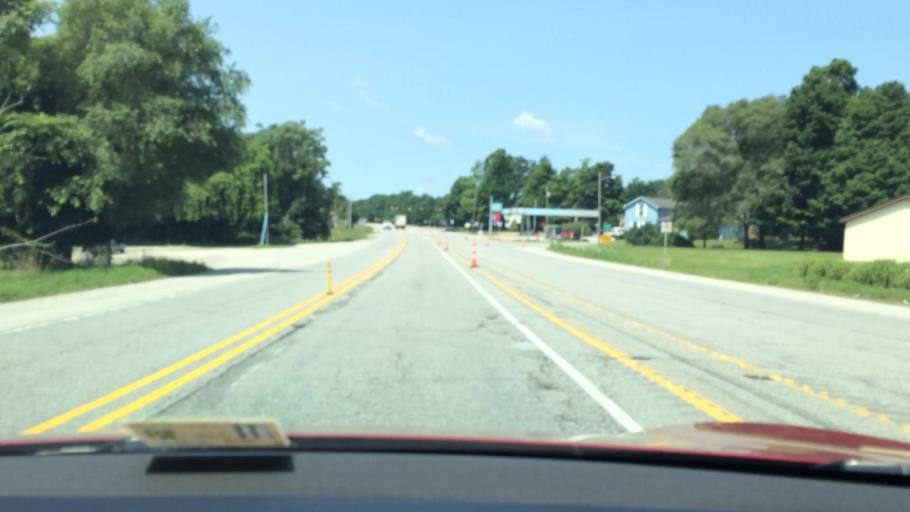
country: US
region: Indiana
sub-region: LaPorte County
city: Hudson Lake
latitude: 41.6714
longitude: -86.6193
